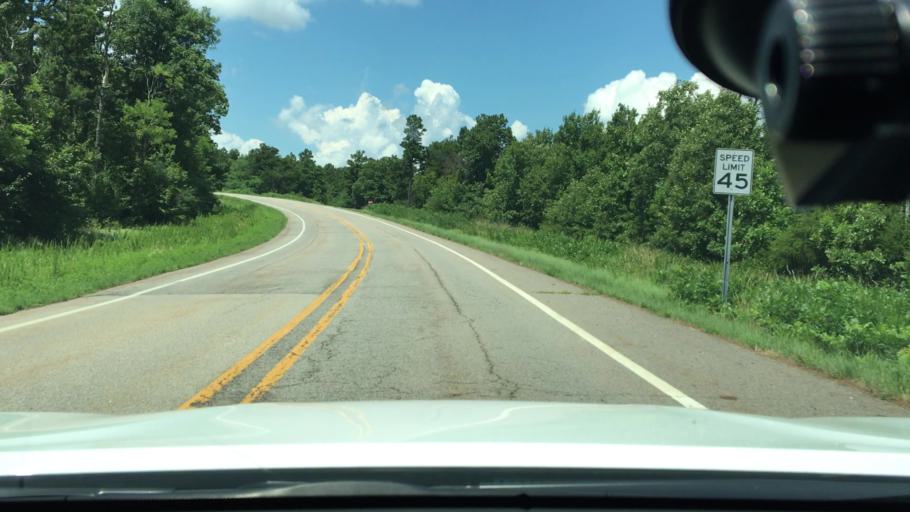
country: US
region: Arkansas
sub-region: Logan County
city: Paris
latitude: 35.1764
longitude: -93.6146
